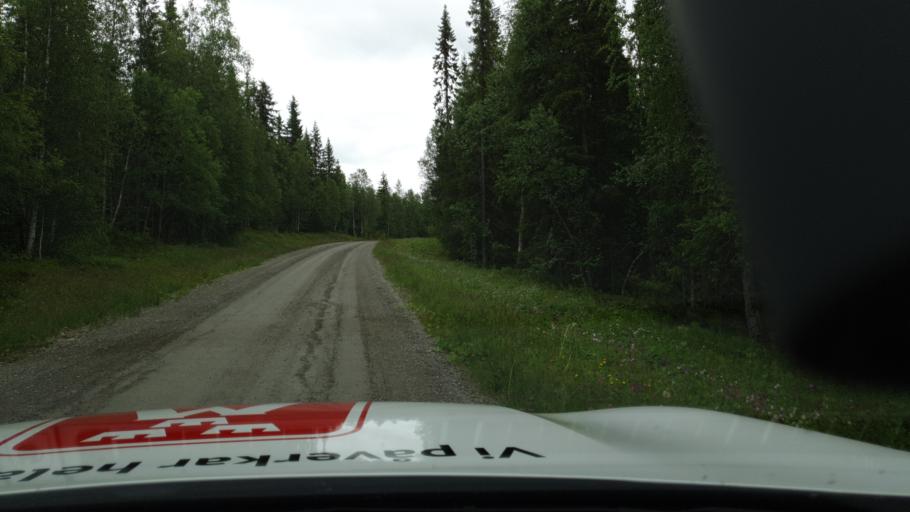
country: SE
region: Vaesterbotten
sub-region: Storumans Kommun
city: Storuman
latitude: 64.7863
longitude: 17.0245
